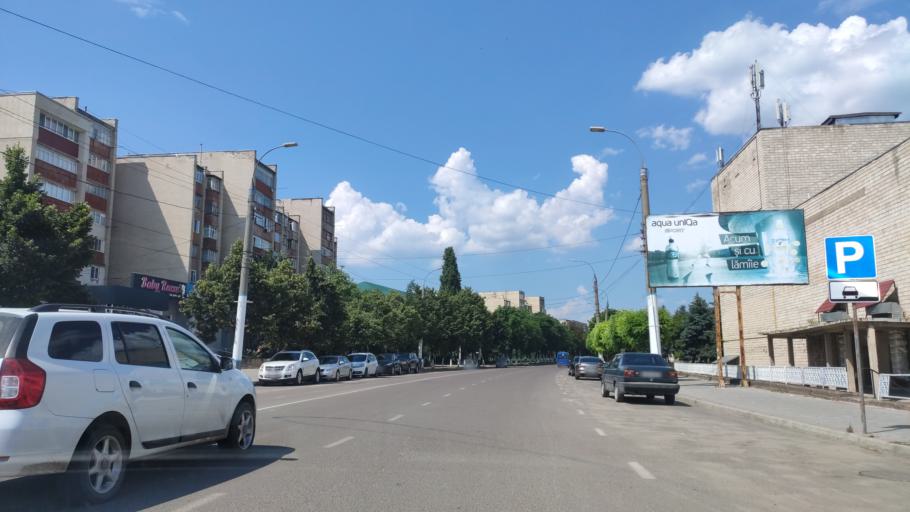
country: MD
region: Raionul Soroca
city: Soroca
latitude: 48.1574
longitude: 28.3020
